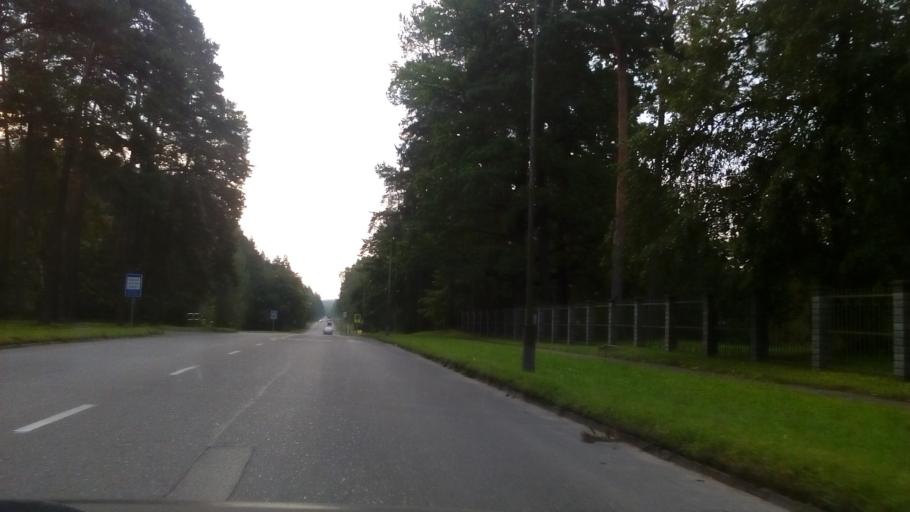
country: LT
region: Alytaus apskritis
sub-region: Alytus
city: Alytus
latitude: 54.3801
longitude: 24.0614
